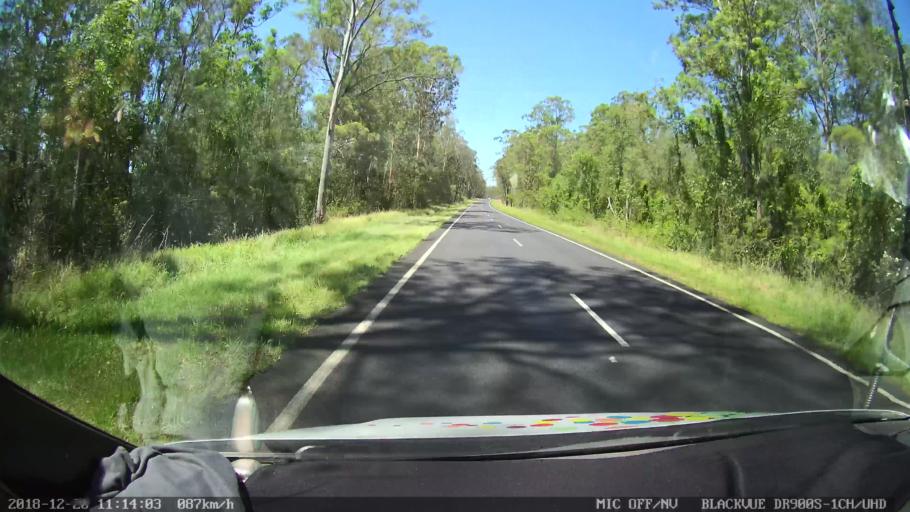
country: AU
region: New South Wales
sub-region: Richmond Valley
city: Casino
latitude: -28.9958
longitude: 153.0107
